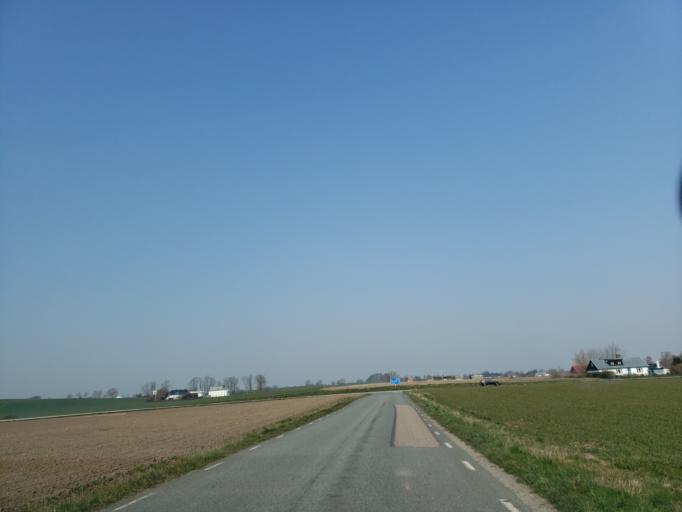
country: SE
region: Skane
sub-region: Simrishamns Kommun
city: Simrishamn
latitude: 55.4652
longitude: 14.2077
